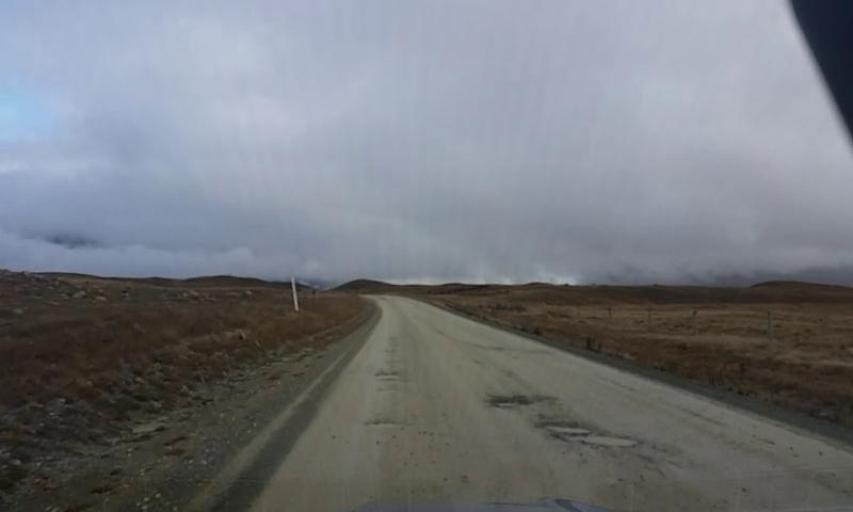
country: NZ
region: Canterbury
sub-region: Ashburton District
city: Methven
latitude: -43.6143
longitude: 171.1519
